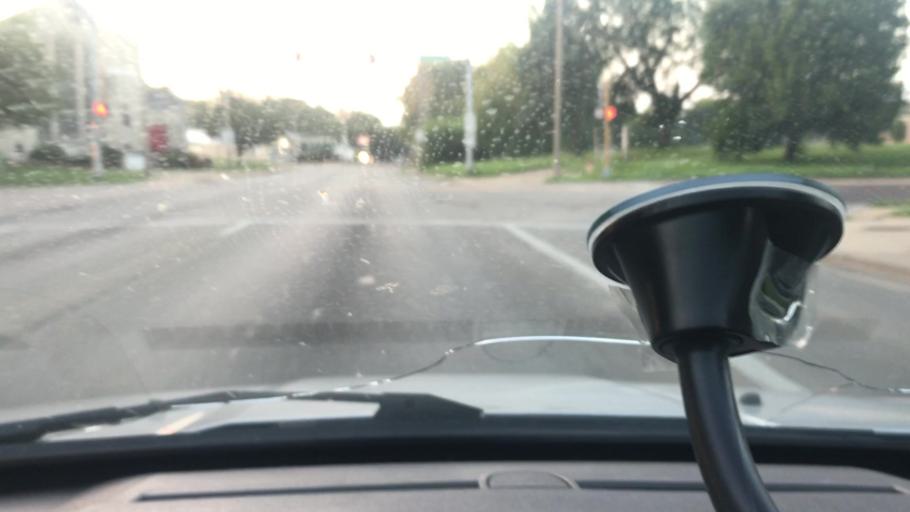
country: US
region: Illinois
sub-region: Tazewell County
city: Pekin
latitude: 40.5675
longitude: -89.6408
